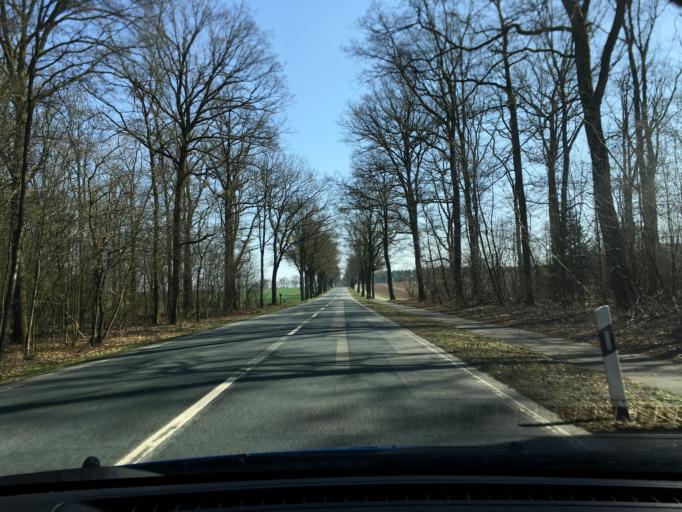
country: DE
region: Lower Saxony
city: Rehlingen
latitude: 53.0861
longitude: 10.2724
